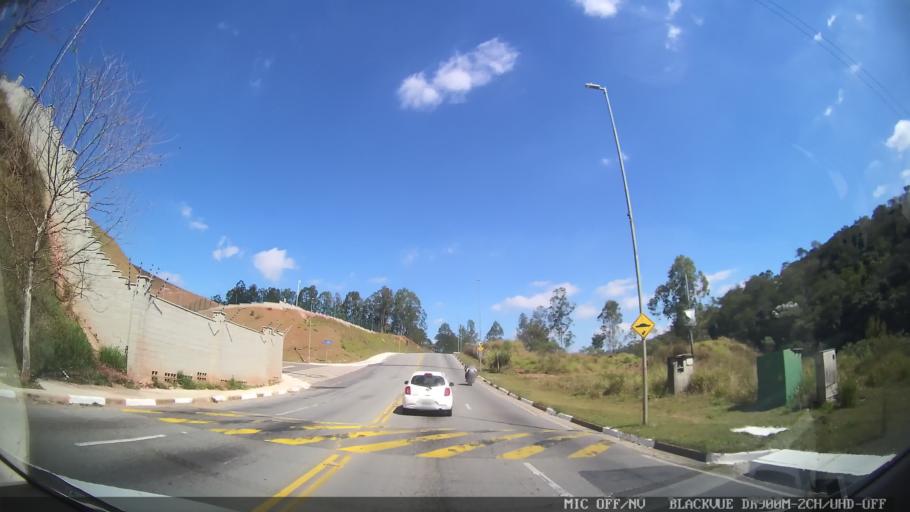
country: BR
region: Sao Paulo
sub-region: Santana De Parnaiba
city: Santana de Parnaiba
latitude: -23.4332
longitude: -46.8301
